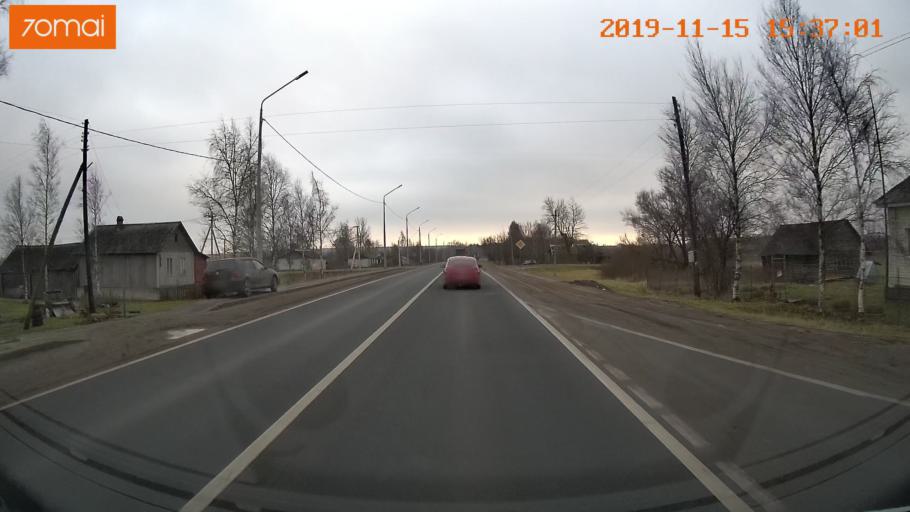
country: RU
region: Jaroslavl
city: Danilov
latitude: 58.0435
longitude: 40.0911
